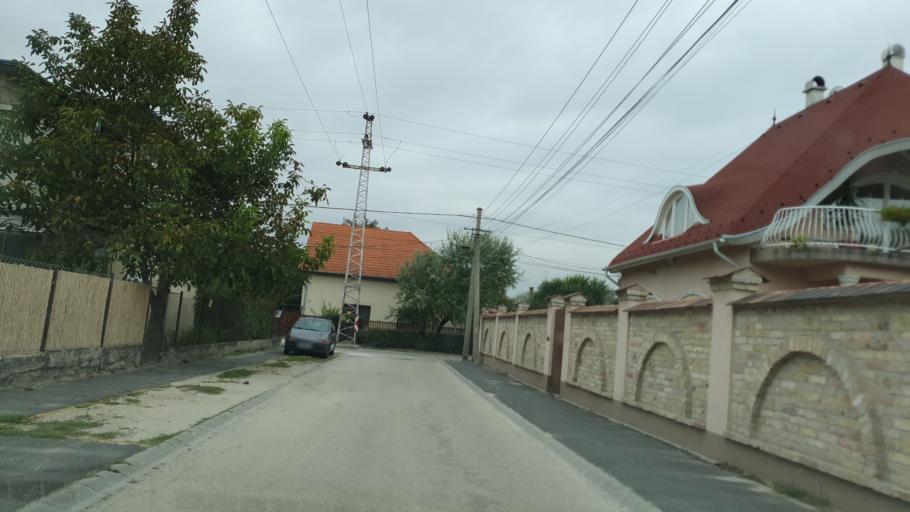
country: HU
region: Budapest
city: Budapest XXIII. keruelet
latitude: 47.3921
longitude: 19.0937
